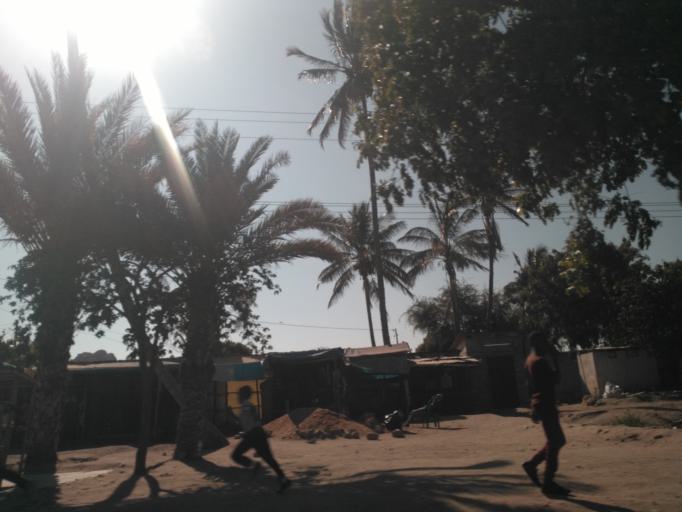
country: TZ
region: Dodoma
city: Dodoma
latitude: -6.1551
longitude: 35.7472
